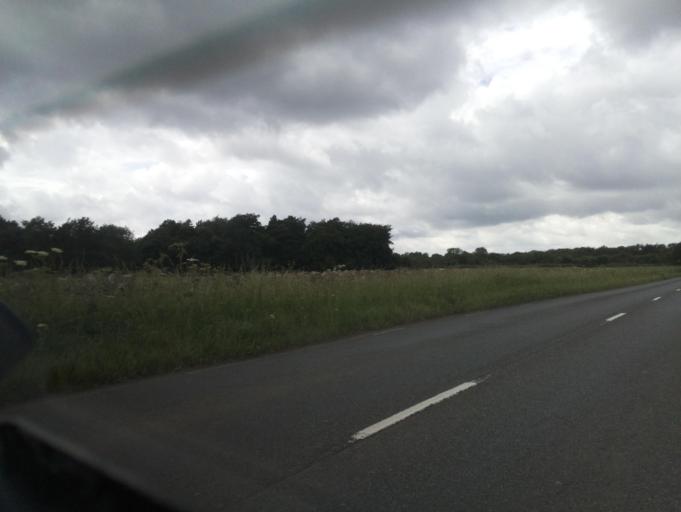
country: GB
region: England
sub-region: South Gloucestershire
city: Cold Ashton
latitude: 51.4269
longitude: -2.4018
